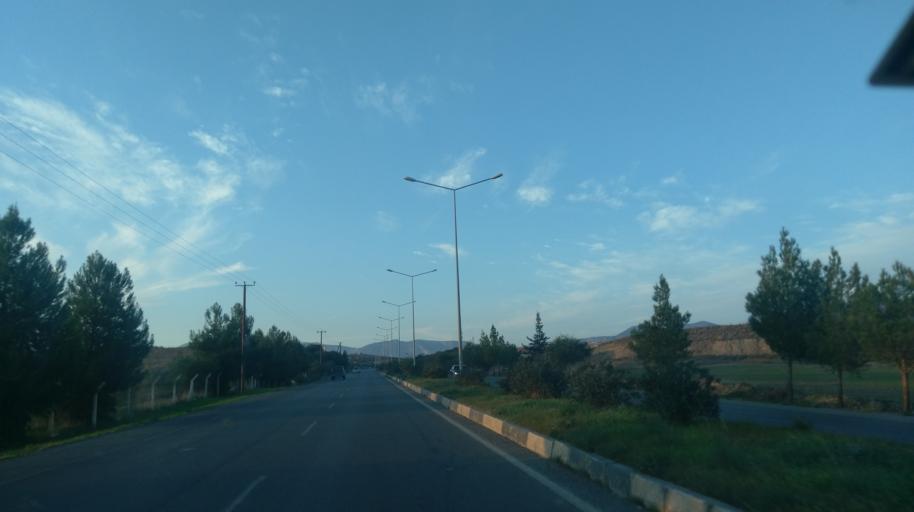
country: CY
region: Lefkosia
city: Nicosia
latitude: 35.2230
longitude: 33.3156
